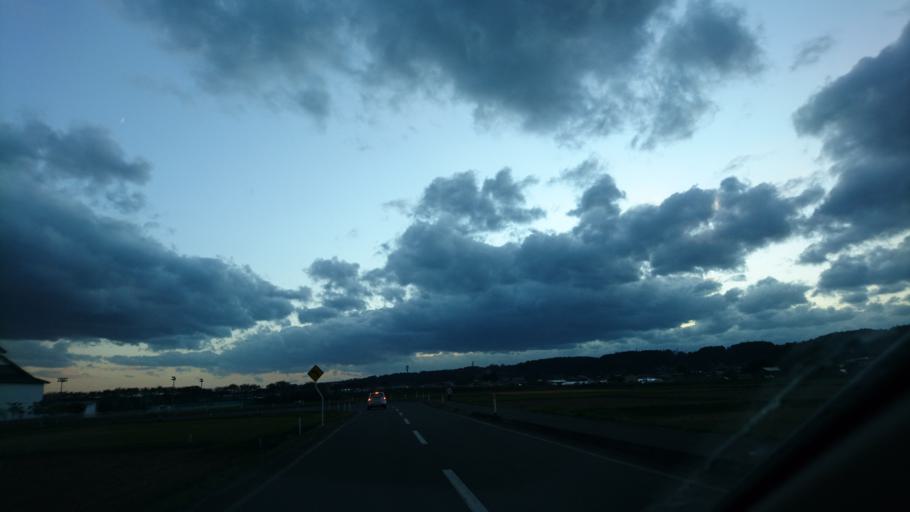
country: JP
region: Iwate
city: Mizusawa
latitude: 39.0604
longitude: 141.1388
